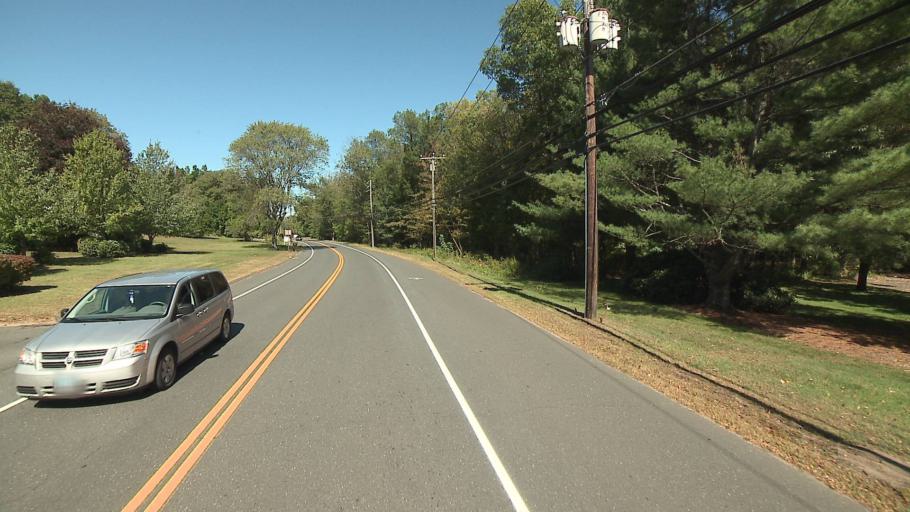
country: US
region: Connecticut
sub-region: Hartford County
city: Salmon Brook
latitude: 41.9317
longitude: -72.7898
